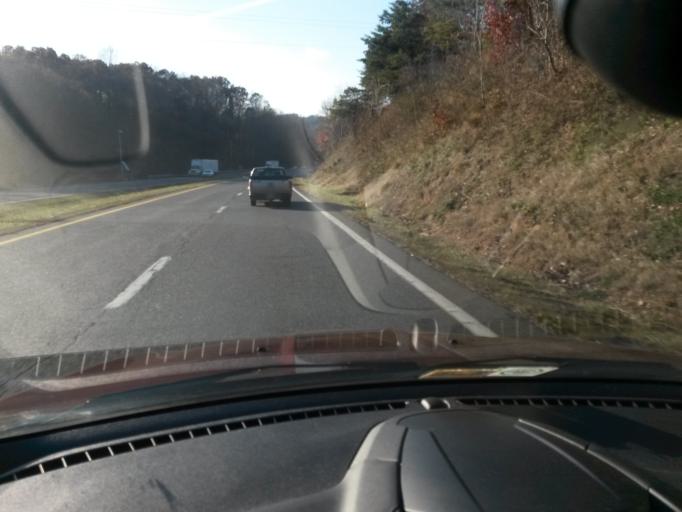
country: US
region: Virginia
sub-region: Campbell County
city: Concord
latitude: 37.3740
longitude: -79.0344
